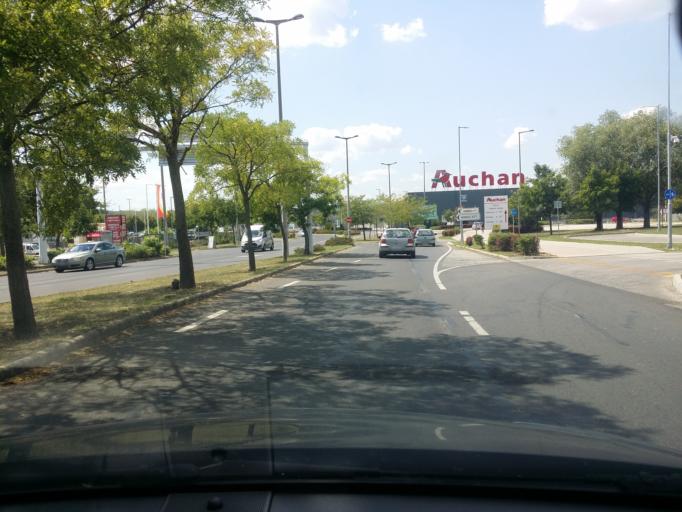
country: HU
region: Pest
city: Budaors
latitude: 47.4555
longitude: 18.9478
